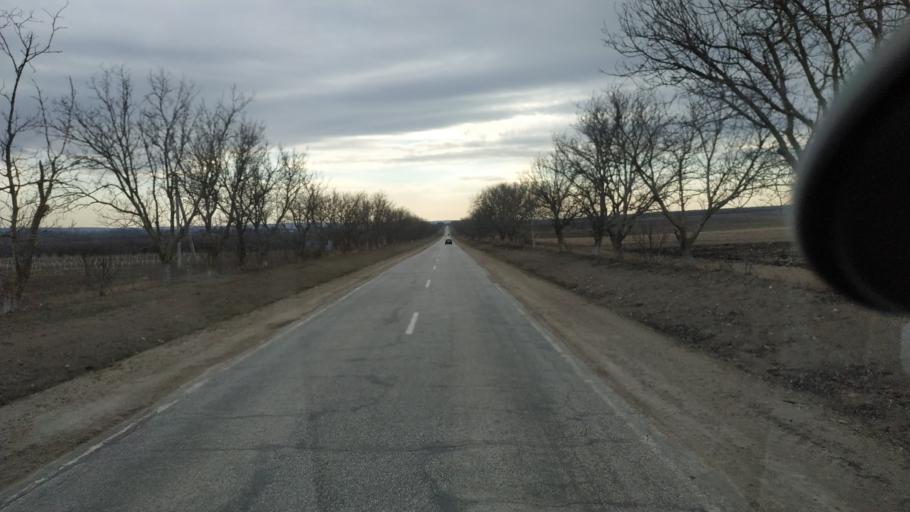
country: MD
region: Criuleni
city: Criuleni
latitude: 47.1923
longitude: 29.1472
